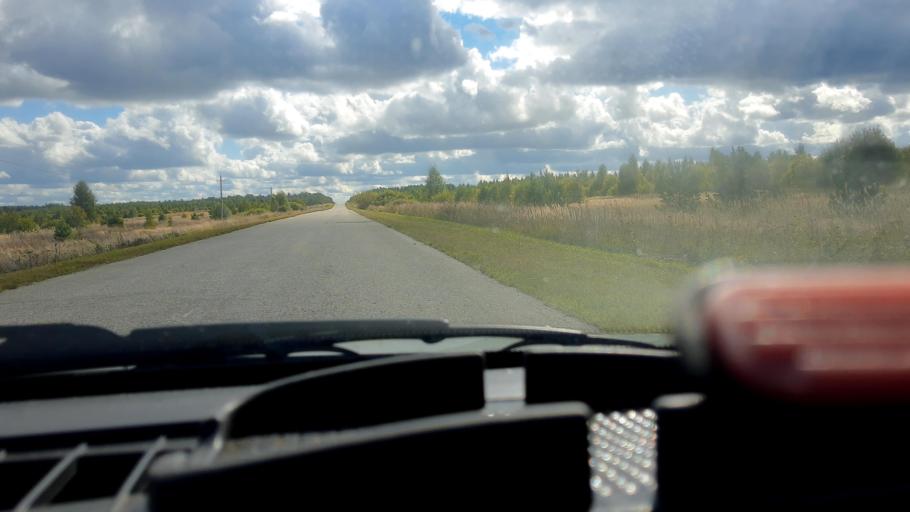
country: RU
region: Mariy-El
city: Kilemary
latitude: 56.9381
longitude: 46.6919
